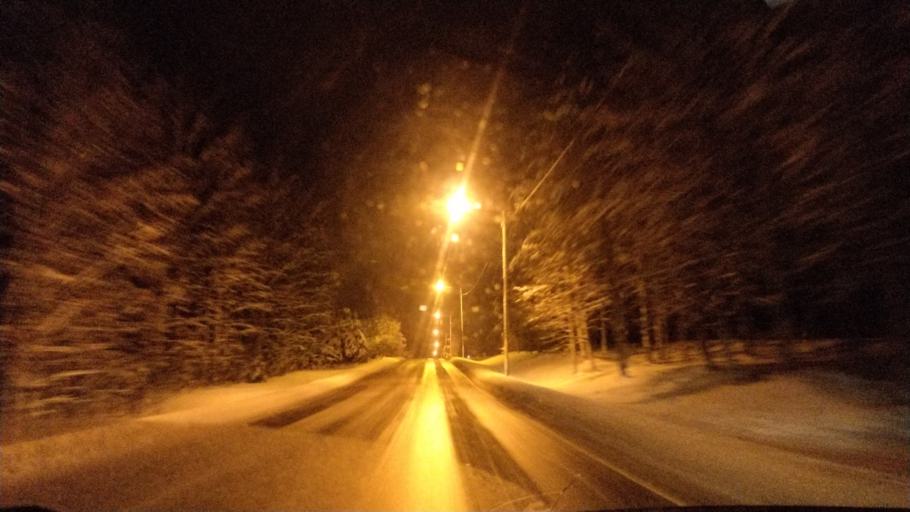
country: FI
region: Lapland
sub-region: Rovaniemi
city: Rovaniemi
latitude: 66.2998
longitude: 25.3533
